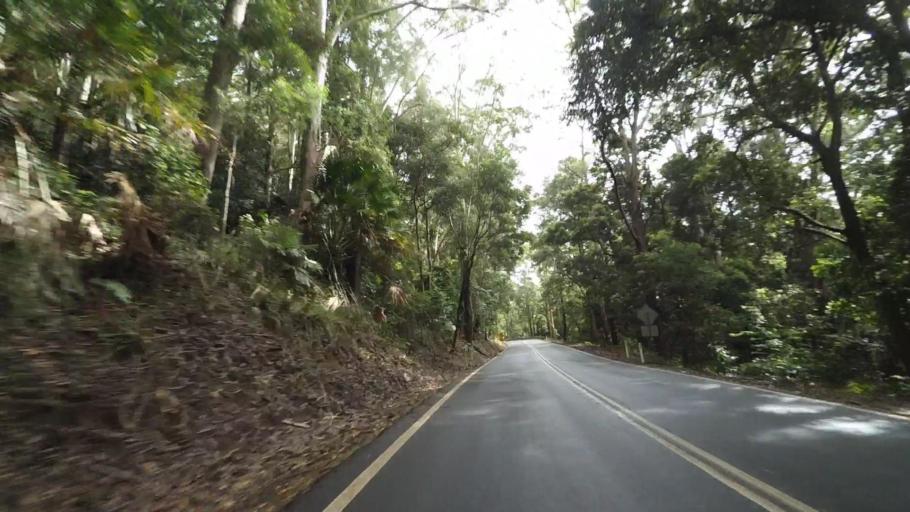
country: AU
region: New South Wales
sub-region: Wollongong
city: Helensburgh
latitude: -34.1977
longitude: 151.0113
